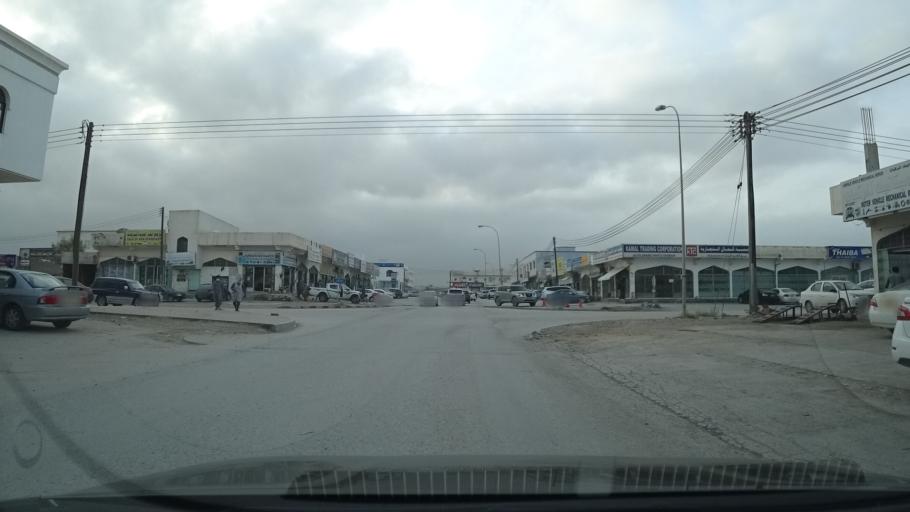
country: OM
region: Zufar
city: Salalah
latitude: 17.0204
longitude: 54.0520
